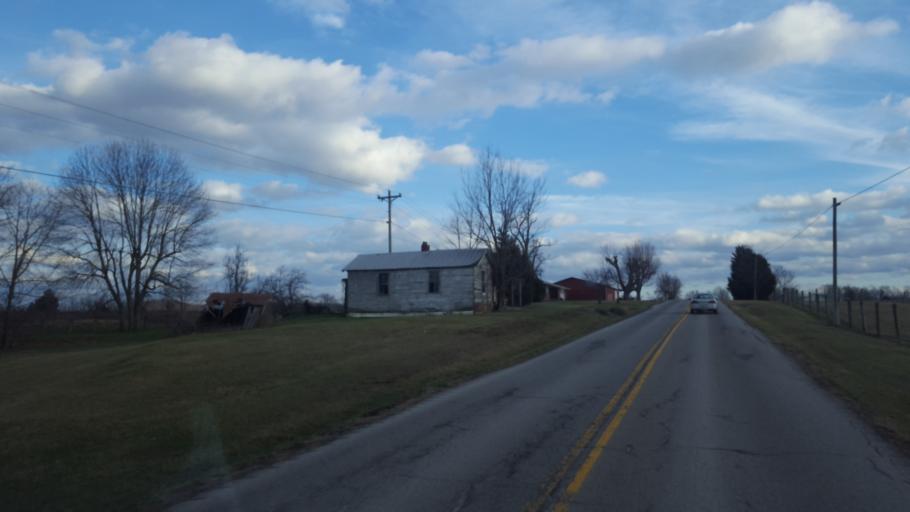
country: US
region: Kentucky
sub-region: Fleming County
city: Flemingsburg
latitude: 38.4856
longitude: -83.6121
